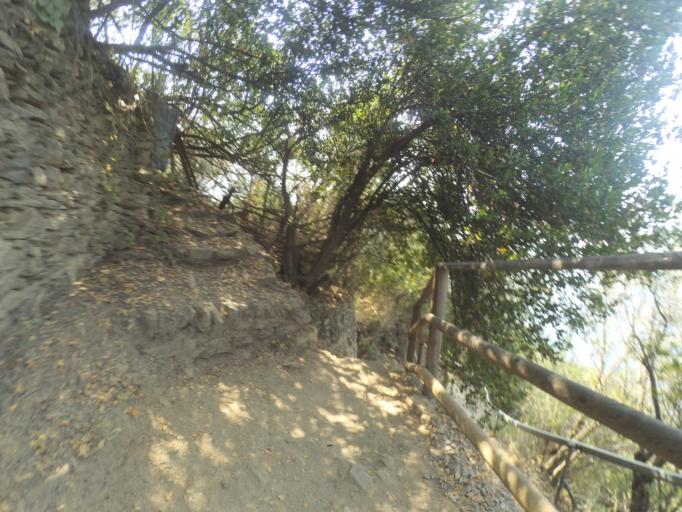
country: IT
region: Liguria
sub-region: Provincia di La Spezia
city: Vernazza
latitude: 44.1383
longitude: 9.6781
